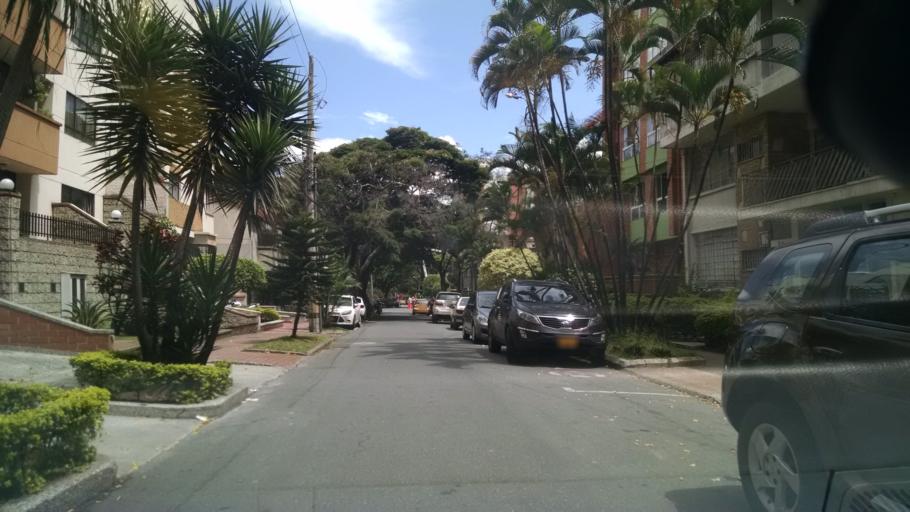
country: CO
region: Antioquia
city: Medellin
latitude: 6.2413
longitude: -75.5926
